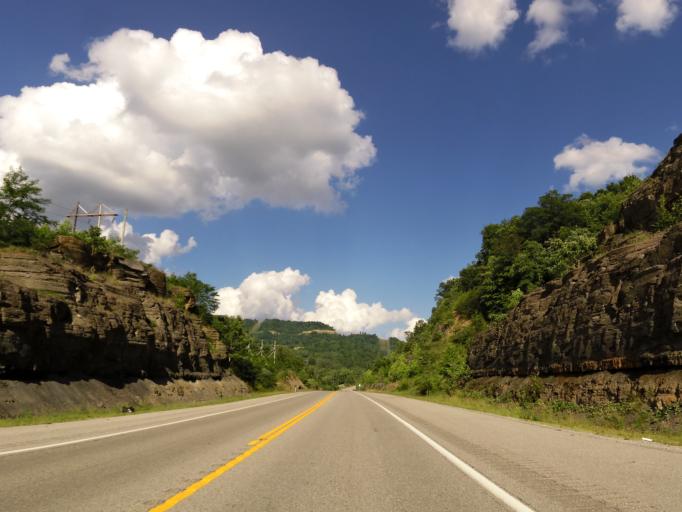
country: US
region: Kentucky
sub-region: Harlan County
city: Harlan
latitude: 36.7807
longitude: -83.2283
